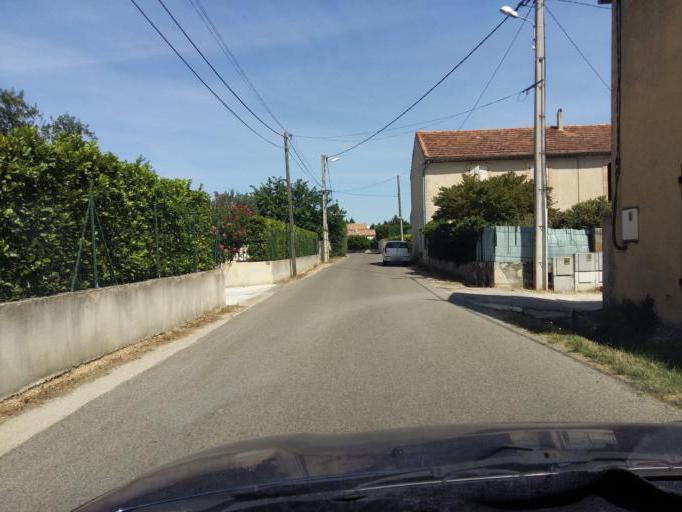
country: FR
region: Provence-Alpes-Cote d'Azur
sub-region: Departement du Vaucluse
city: Camaret-sur-Aigues
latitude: 44.1656
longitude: 4.8678
